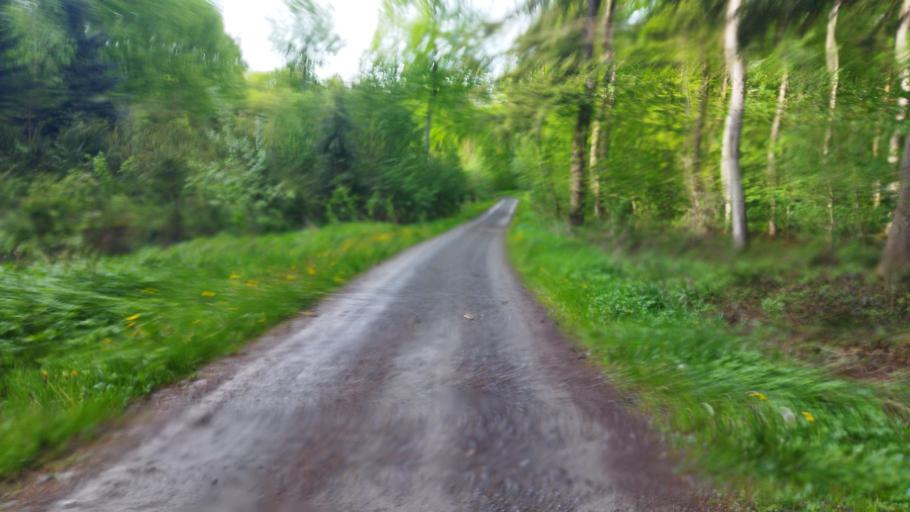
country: DE
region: Baden-Wuerttemberg
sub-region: Regierungsbezirk Stuttgart
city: Mundelsheim
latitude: 49.0258
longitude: 9.2264
